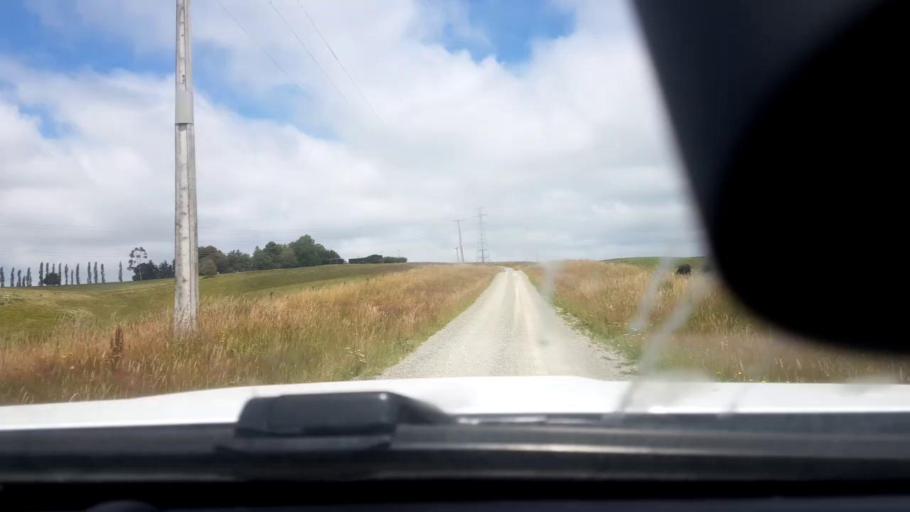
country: NZ
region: Canterbury
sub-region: Timaru District
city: Pleasant Point
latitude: -44.1518
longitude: 171.1525
